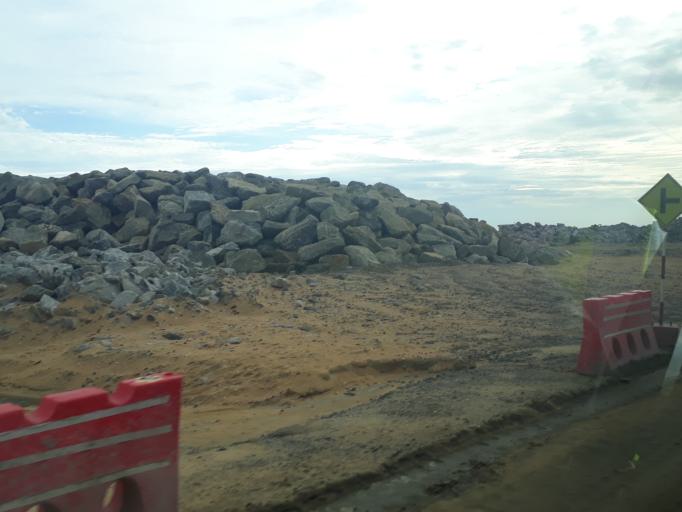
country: LK
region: Western
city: Colombo
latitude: 6.9383
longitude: 79.8360
